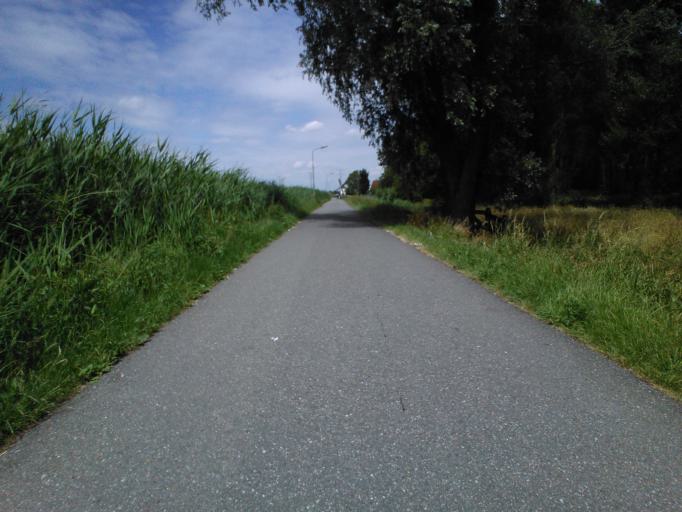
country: NL
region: South Holland
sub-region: Gemeente Alblasserdam
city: Alblasserdam
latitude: 51.8675
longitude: 4.6737
